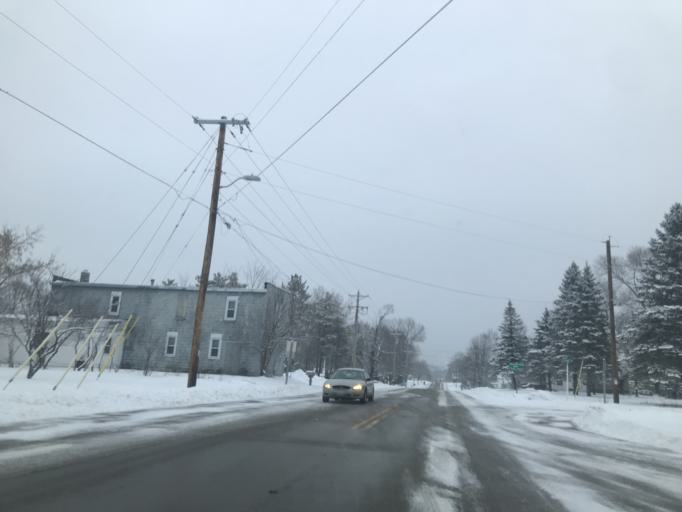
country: US
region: Wisconsin
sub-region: Oconto County
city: Oconto Falls
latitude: 44.8714
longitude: -88.1571
